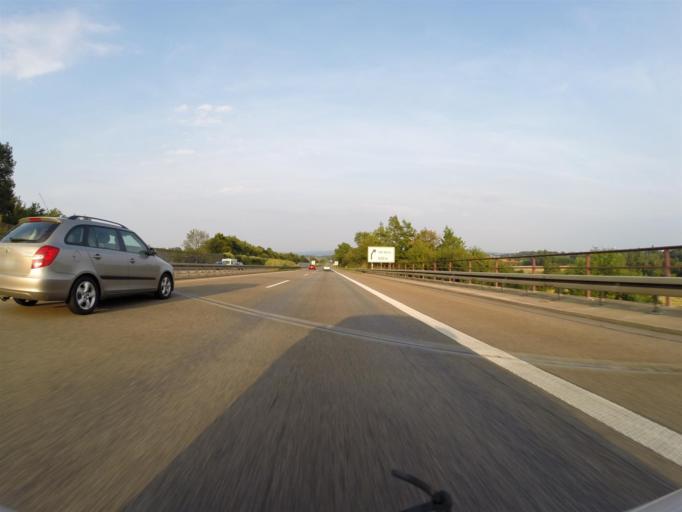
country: DE
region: Hesse
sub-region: Regierungsbezirk Kassel
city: Baunatal
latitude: 51.2672
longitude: 9.4334
